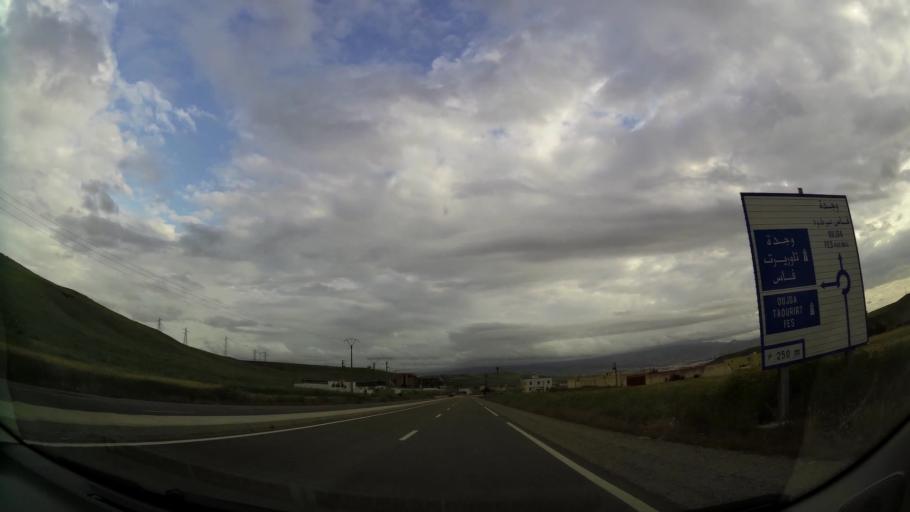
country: MA
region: Taza-Al Hoceima-Taounate
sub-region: Taza
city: Taza
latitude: 34.2737
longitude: -3.9565
